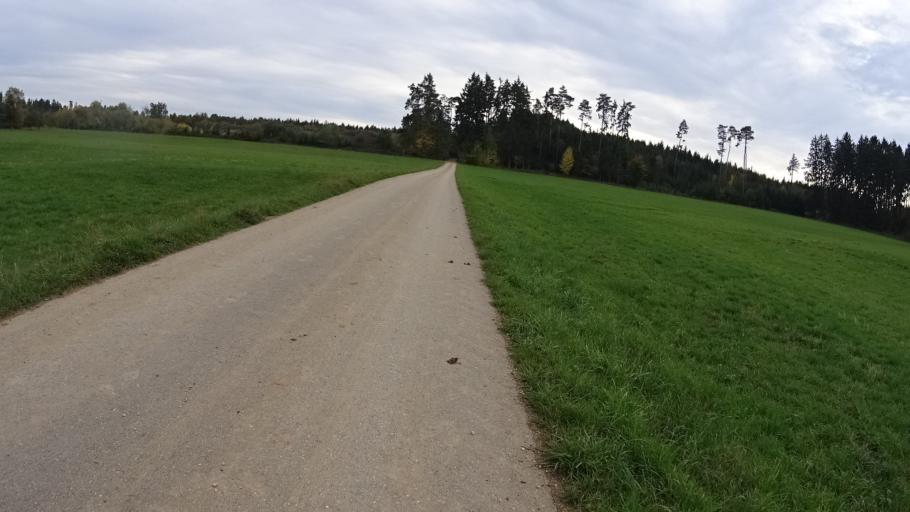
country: DE
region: Bavaria
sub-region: Upper Bavaria
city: Hitzhofen
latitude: 48.8529
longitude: 11.2995
